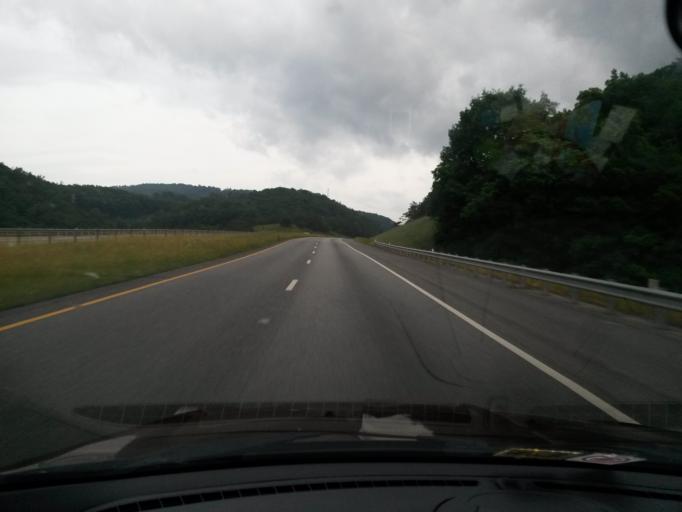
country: US
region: Virginia
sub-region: City of Covington
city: Covington
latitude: 37.7911
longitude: -80.0358
